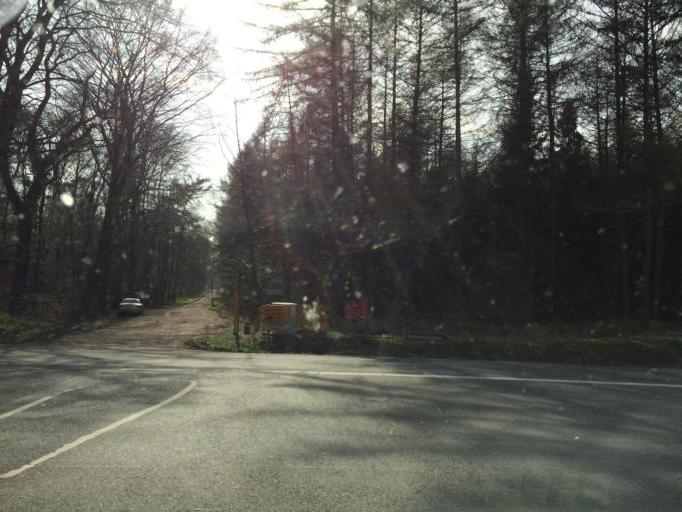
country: DE
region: North Rhine-Westphalia
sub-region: Regierungsbezirk Munster
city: Klein Reken
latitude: 51.7734
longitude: 7.1084
